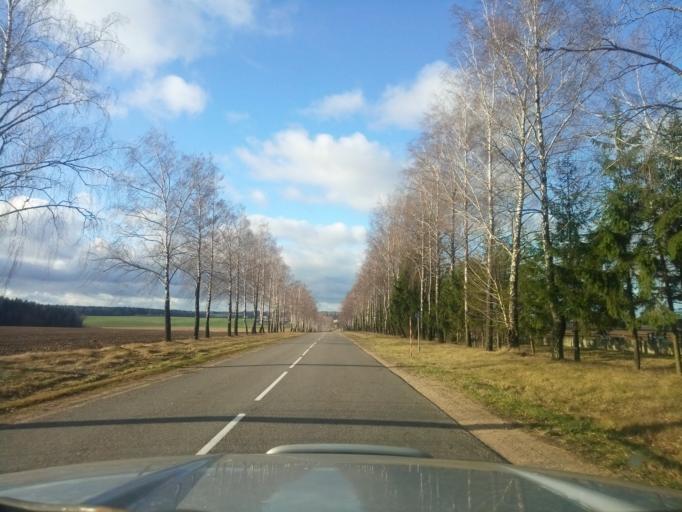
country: BY
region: Minsk
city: Tsimkavichy
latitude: 53.1749
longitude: 26.9828
